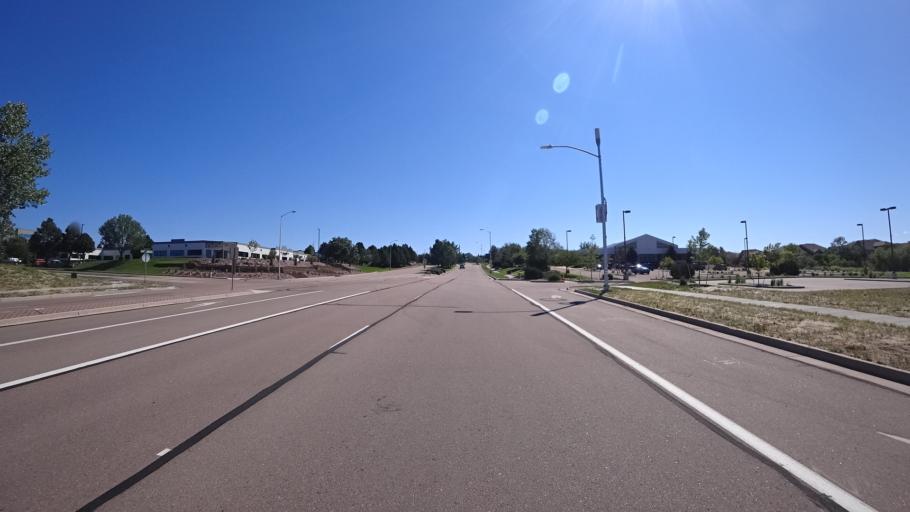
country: US
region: Colorado
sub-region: El Paso County
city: Air Force Academy
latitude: 38.9564
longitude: -104.7905
